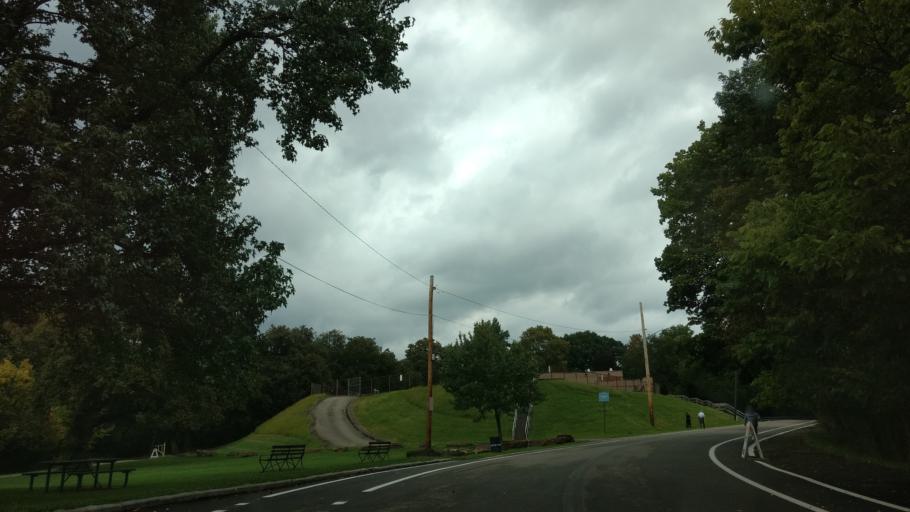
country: US
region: Pennsylvania
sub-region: Allegheny County
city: Bellevue
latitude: 40.4788
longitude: -80.0191
